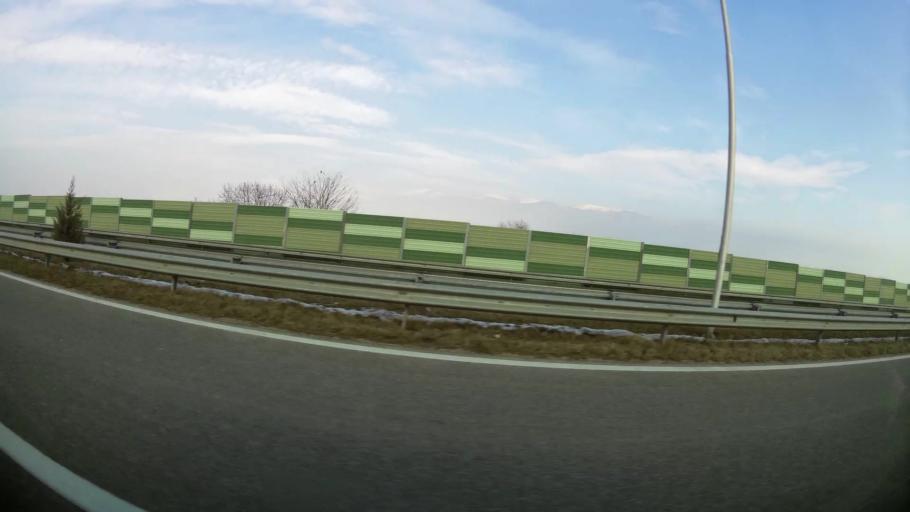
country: MK
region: Suto Orizari
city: Suto Orizare
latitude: 42.0461
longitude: 21.4401
